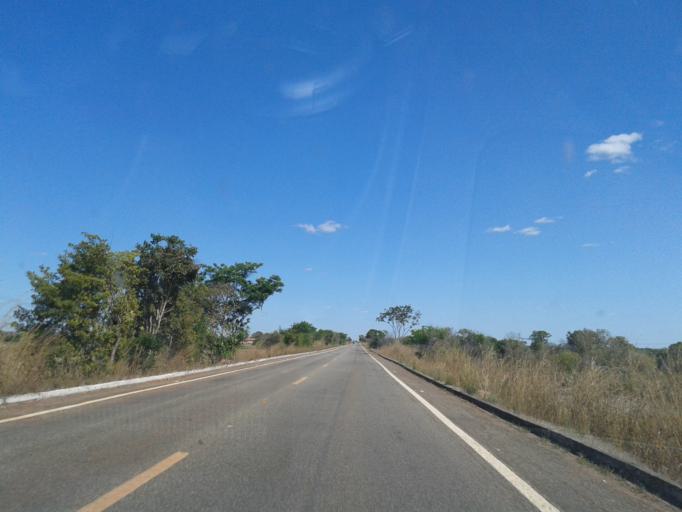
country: BR
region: Goias
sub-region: Sao Miguel Do Araguaia
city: Sao Miguel do Araguaia
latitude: -13.5910
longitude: -50.3174
